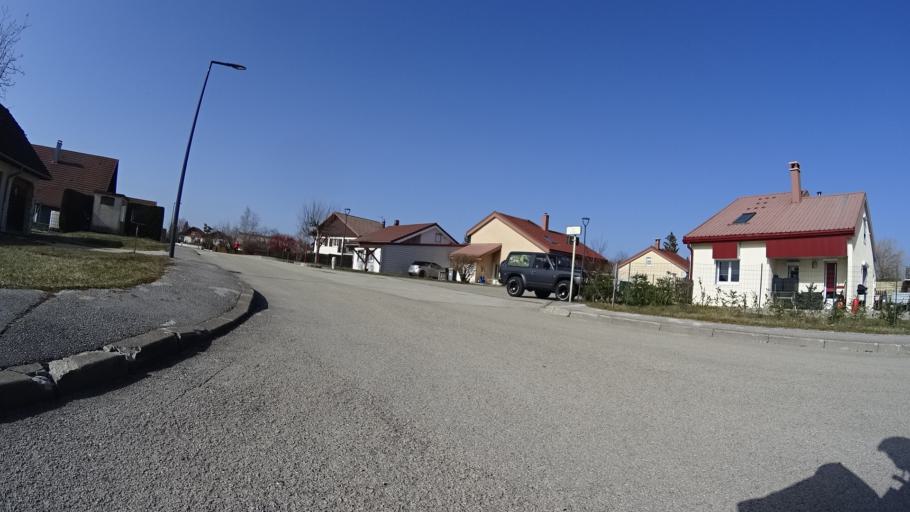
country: FR
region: Franche-Comte
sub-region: Departement du Doubs
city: Frasne
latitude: 46.8495
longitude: 6.1604
